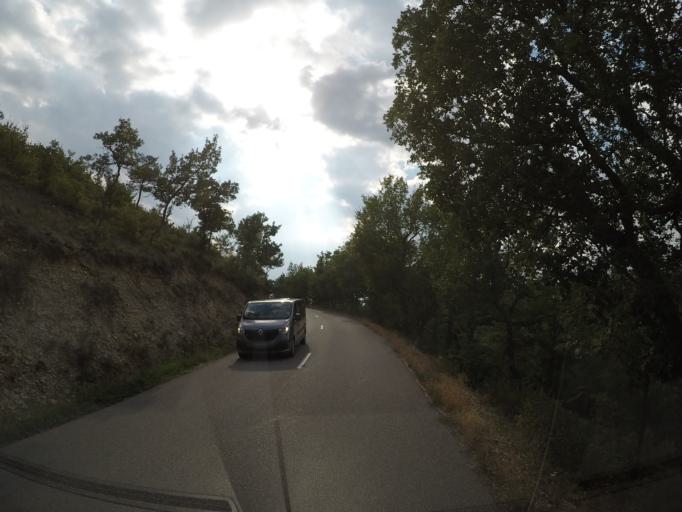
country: FR
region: Provence-Alpes-Cote d'Azur
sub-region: Departement des Alpes-de-Haute-Provence
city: Riez
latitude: 43.8282
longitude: 6.0426
